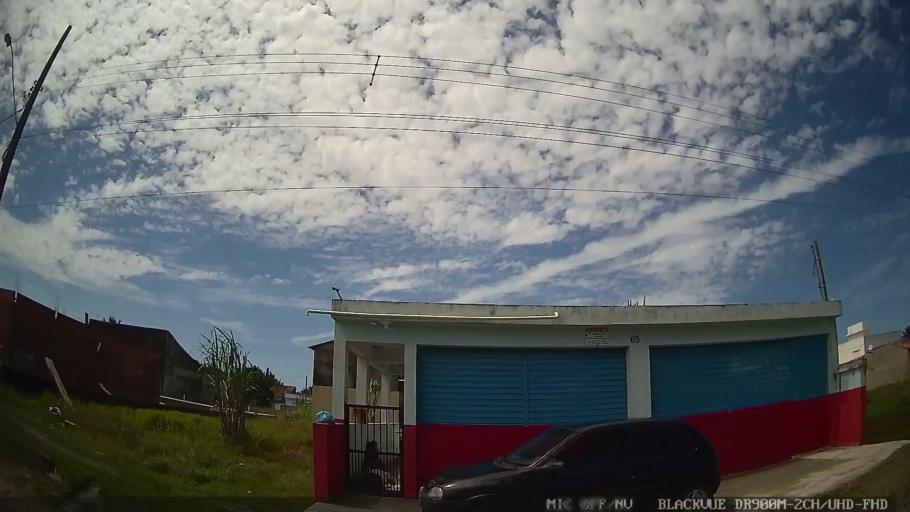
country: BR
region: Sao Paulo
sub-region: Iguape
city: Iguape
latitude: -24.7221
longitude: -47.5062
